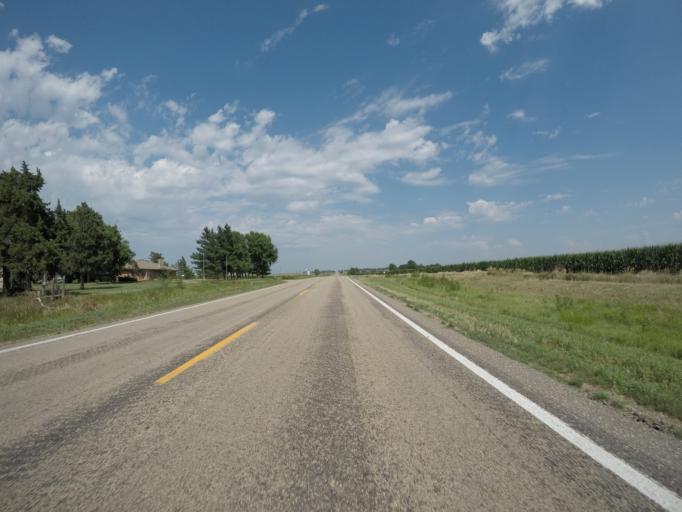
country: US
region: Nebraska
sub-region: Thayer County
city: Hebron
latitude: 40.0167
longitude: -97.6394
